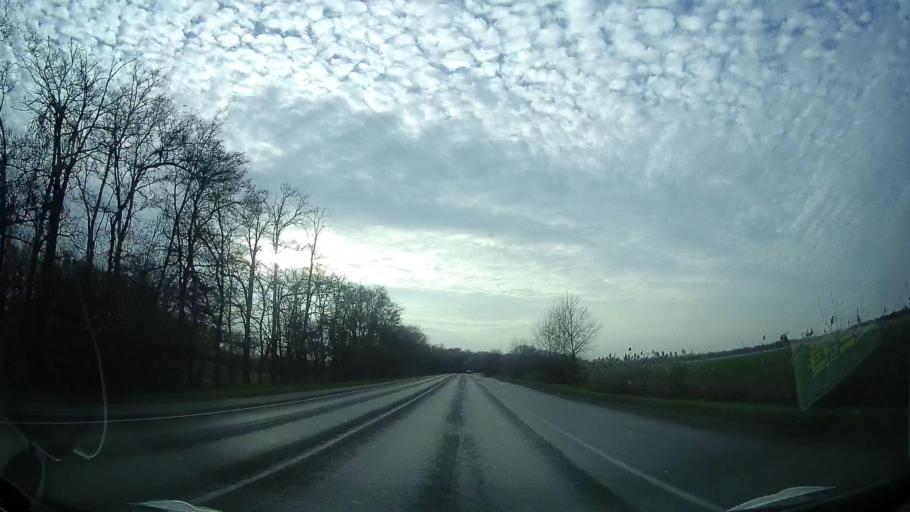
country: RU
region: Rostov
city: Bagayevskaya
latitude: 47.1641
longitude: 40.2633
